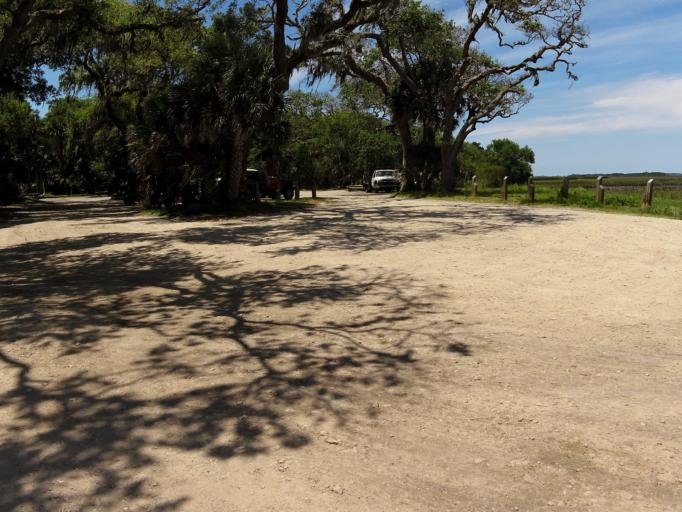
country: US
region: Florida
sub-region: Duval County
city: Atlantic Beach
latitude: 30.4443
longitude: -81.4619
